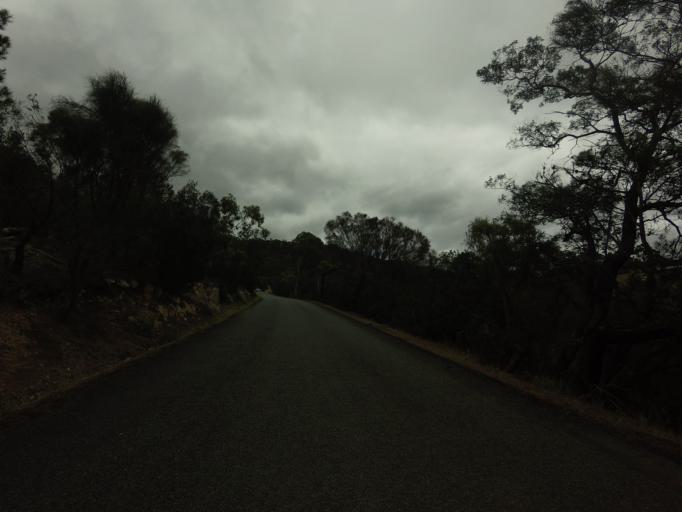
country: AU
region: Tasmania
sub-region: Clarence
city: Cambridge
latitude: -42.7857
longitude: 147.4127
